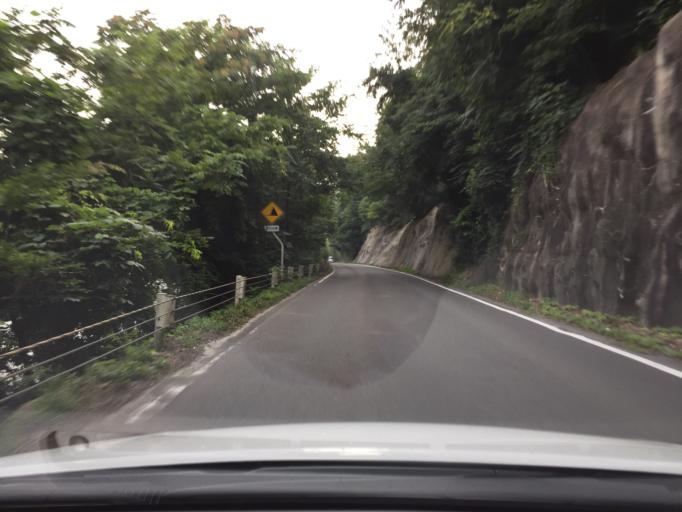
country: JP
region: Fukushima
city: Fukushima-shi
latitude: 37.7198
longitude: 140.4805
